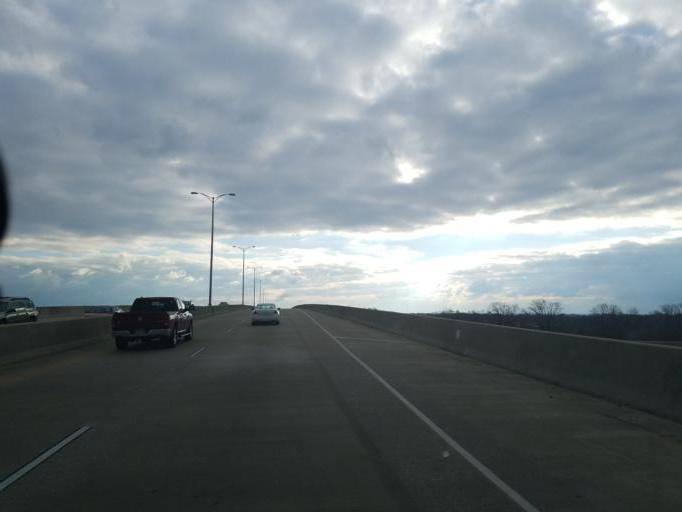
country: US
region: Illinois
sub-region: Madison County
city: Mitchell
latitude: 38.7657
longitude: -90.1376
